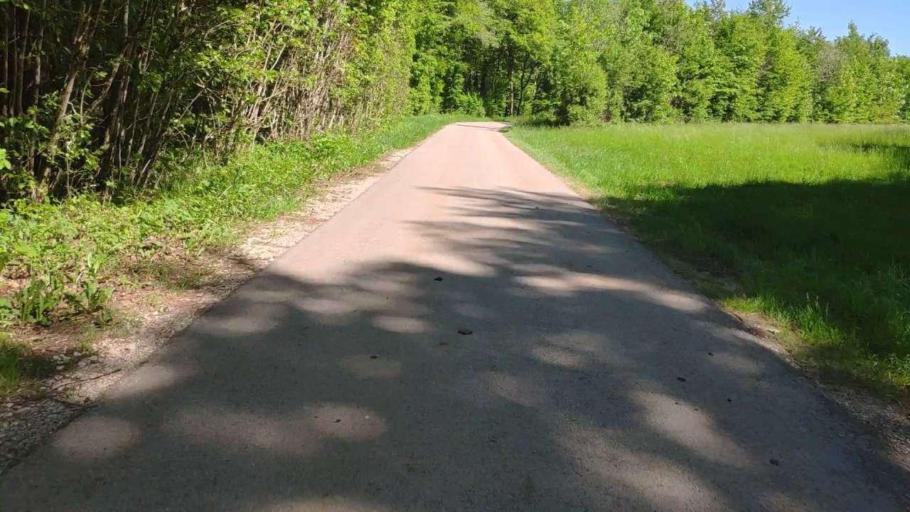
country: FR
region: Franche-Comte
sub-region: Departement du Jura
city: Poligny
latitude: 46.7457
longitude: 5.7740
